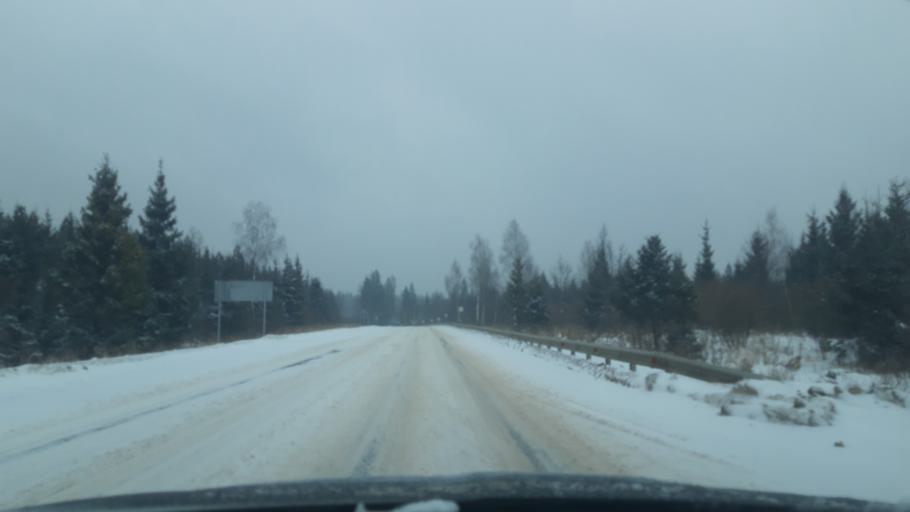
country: RU
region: Moskovskaya
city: Avtopoligon
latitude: 56.2637
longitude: 37.2658
